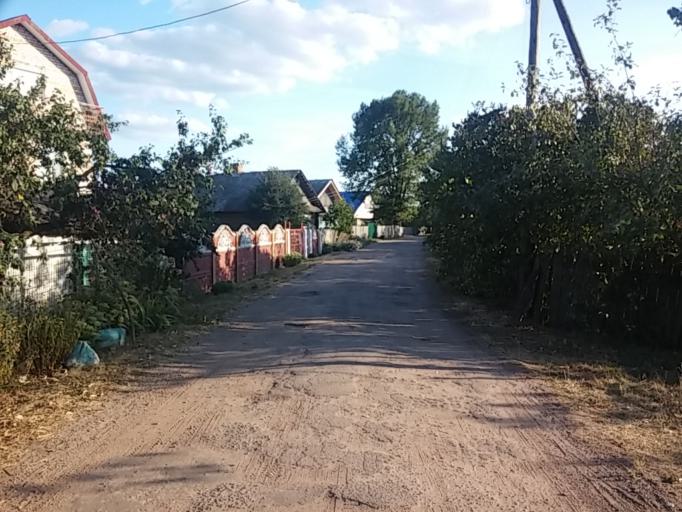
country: BY
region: Minsk
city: Chervyen'
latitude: 53.7779
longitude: 28.2671
